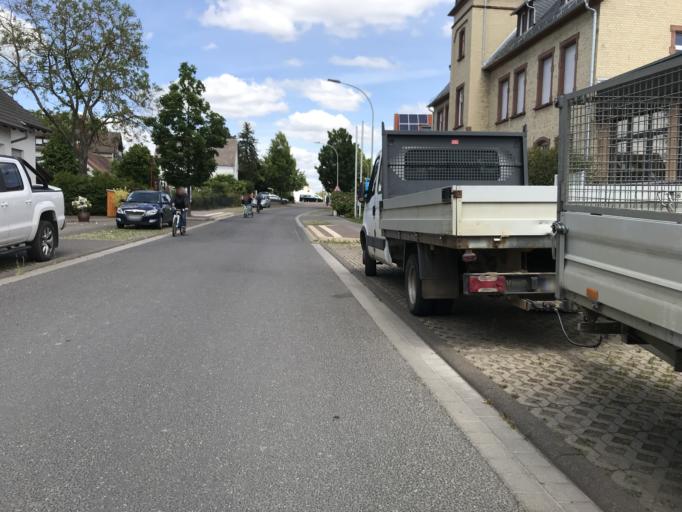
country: DE
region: Hesse
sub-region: Regierungsbezirk Darmstadt
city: Butzbach
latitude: 50.4025
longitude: 8.6711
